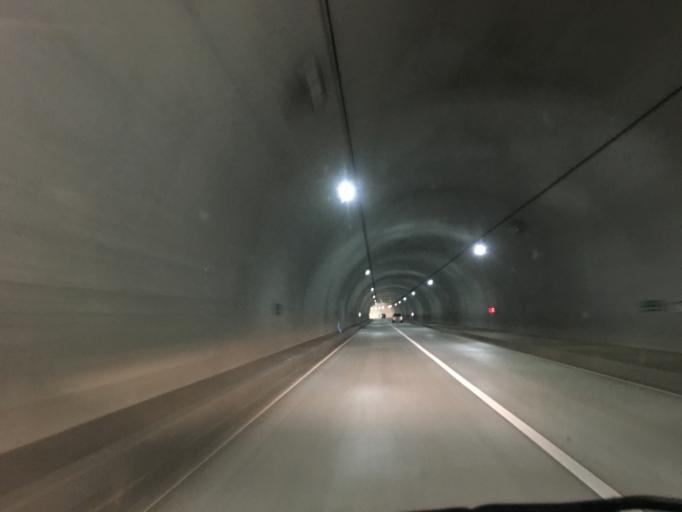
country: JP
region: Fukushima
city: Hobaramachi
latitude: 37.7384
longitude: 140.6066
